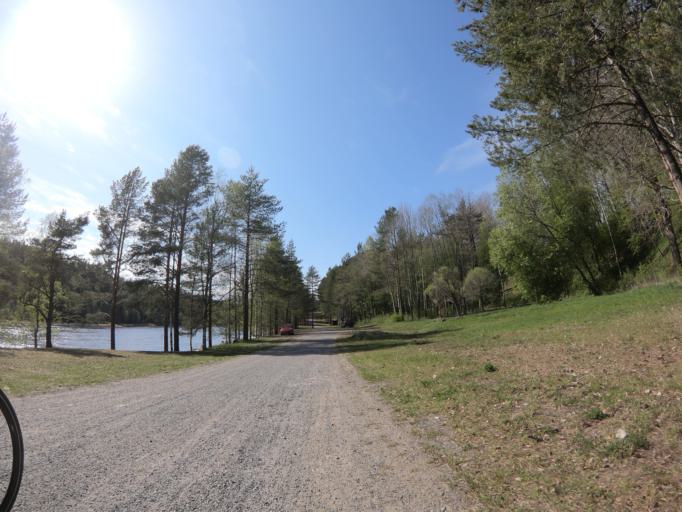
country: SE
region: Vaesterbotten
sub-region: Umea Kommun
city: Roback
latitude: 63.8295
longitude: 20.1697
